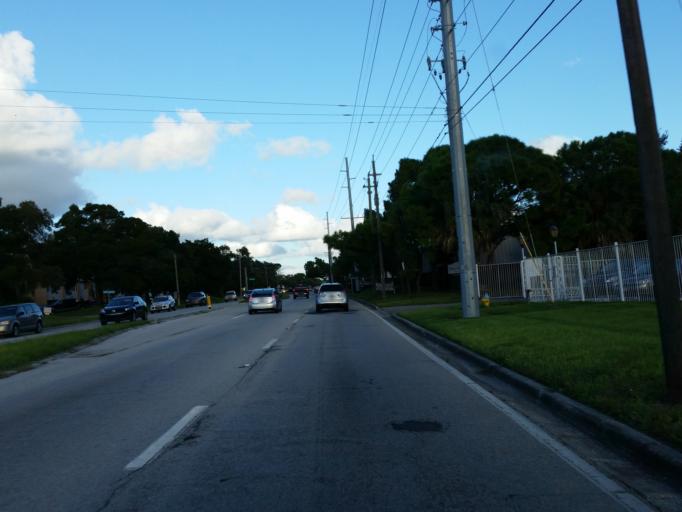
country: US
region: Florida
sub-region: Hillsborough County
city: Town 'n' Country
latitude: 27.9817
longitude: -82.5614
